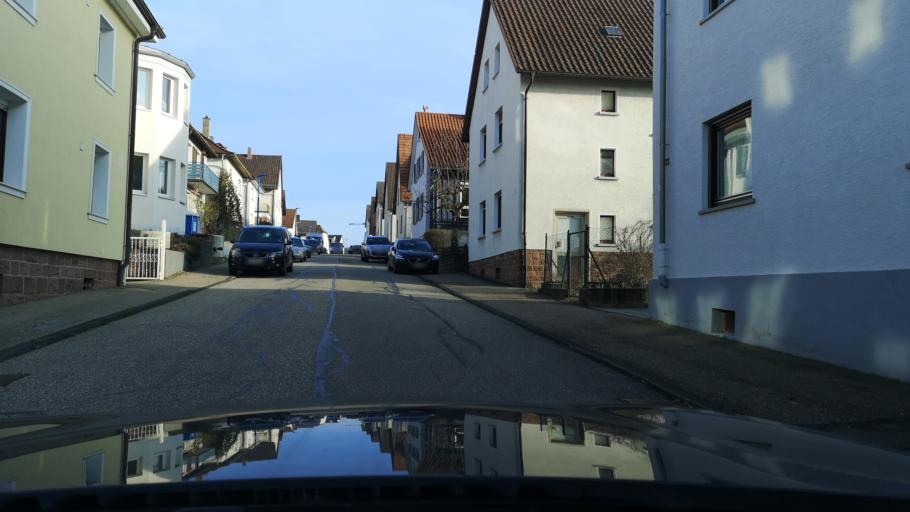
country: DE
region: Baden-Wuerttemberg
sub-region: Karlsruhe Region
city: Ettlingen
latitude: 48.9329
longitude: 8.4648
